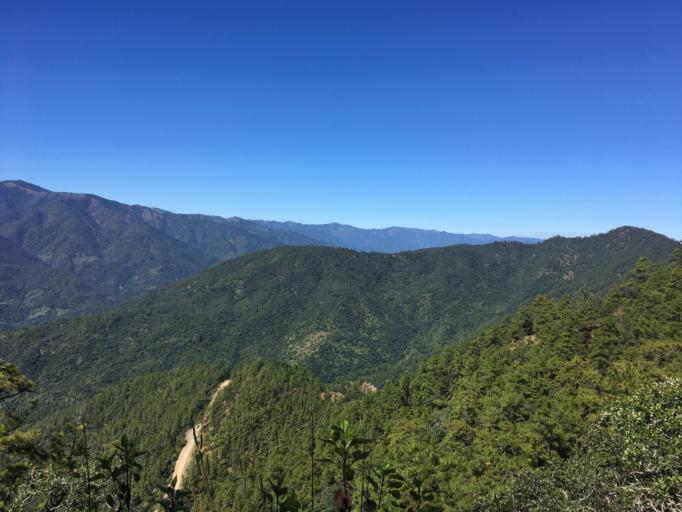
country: MM
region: Chin
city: Hakha
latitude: 22.2716
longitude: 93.6395
